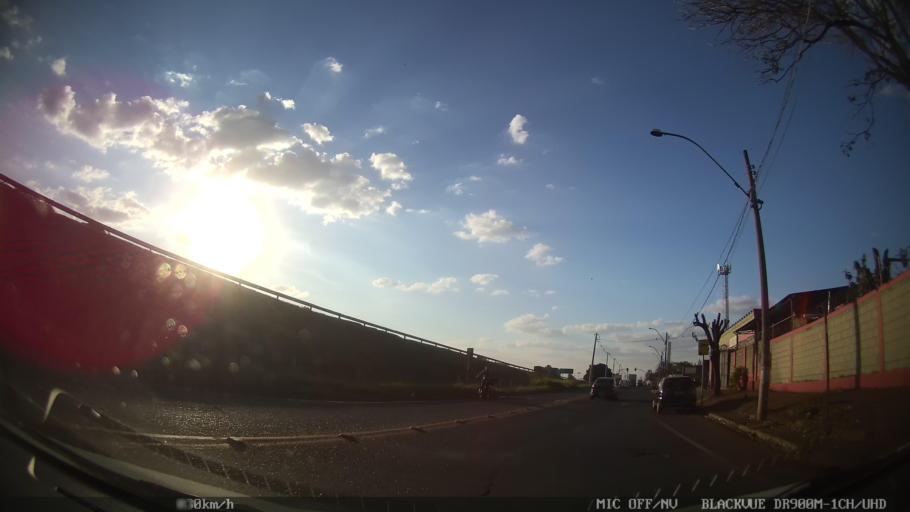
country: BR
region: Sao Paulo
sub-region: Ribeirao Preto
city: Ribeirao Preto
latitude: -21.1849
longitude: -47.7595
